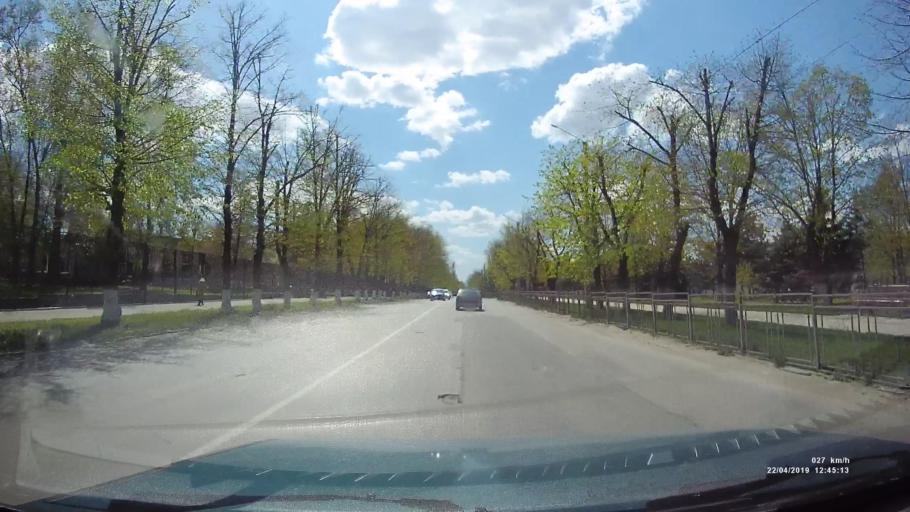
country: RU
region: Rostov
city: Azov
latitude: 47.1049
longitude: 39.4153
